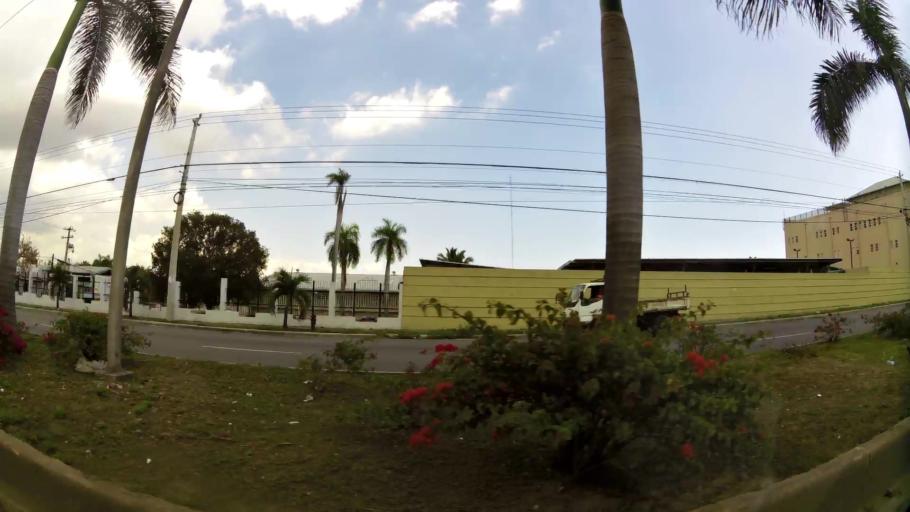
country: DO
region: Santo Domingo
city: Santo Domingo Oeste
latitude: 18.4950
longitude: -69.9994
